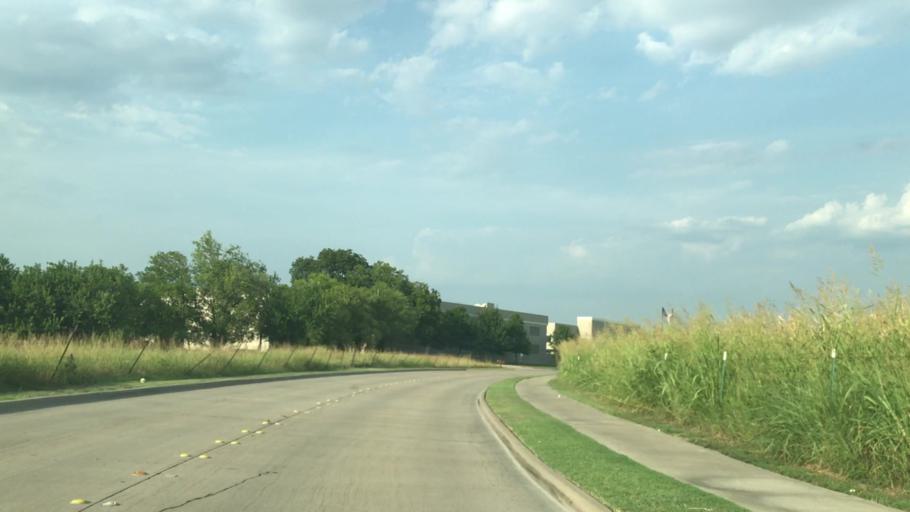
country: US
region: Texas
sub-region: Rockwall County
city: Rockwall
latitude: 32.9210
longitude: -96.4492
